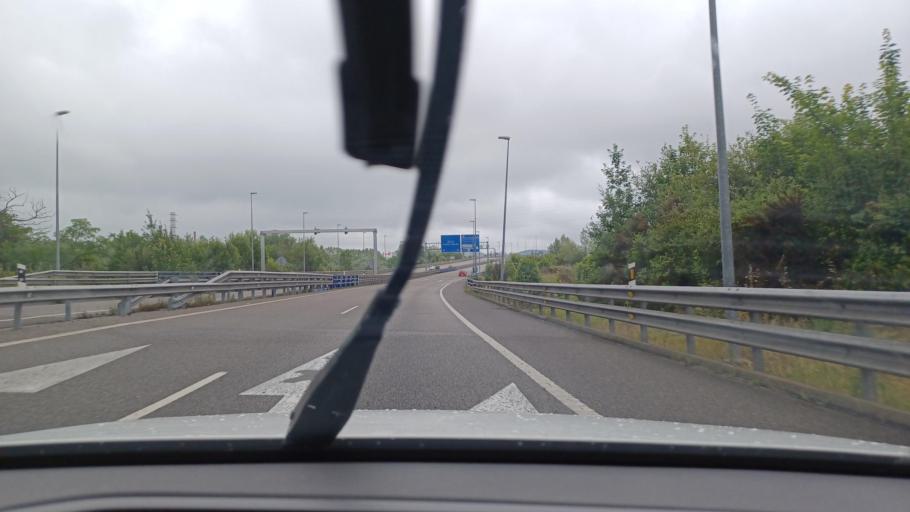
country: ES
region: Asturias
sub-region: Province of Asturias
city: Lugones
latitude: 43.4118
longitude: -5.8189
